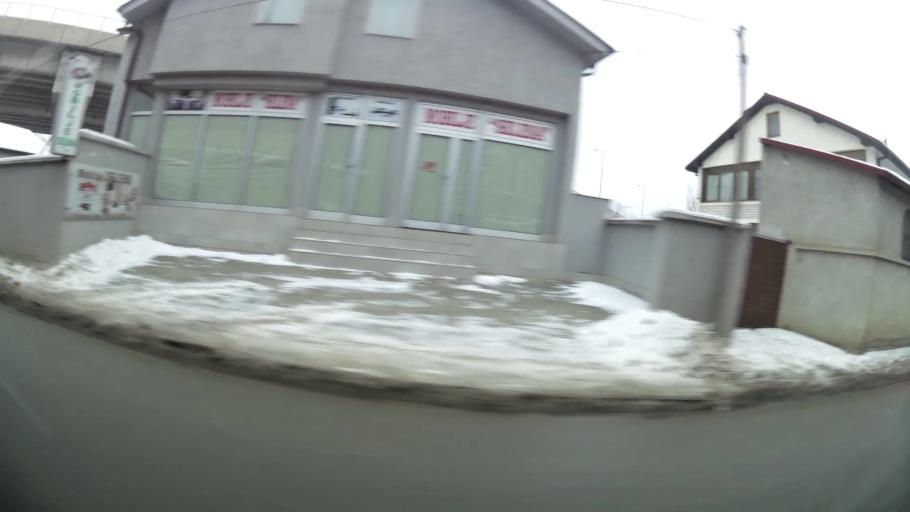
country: MK
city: Kondovo
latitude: 42.0097
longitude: 21.3237
